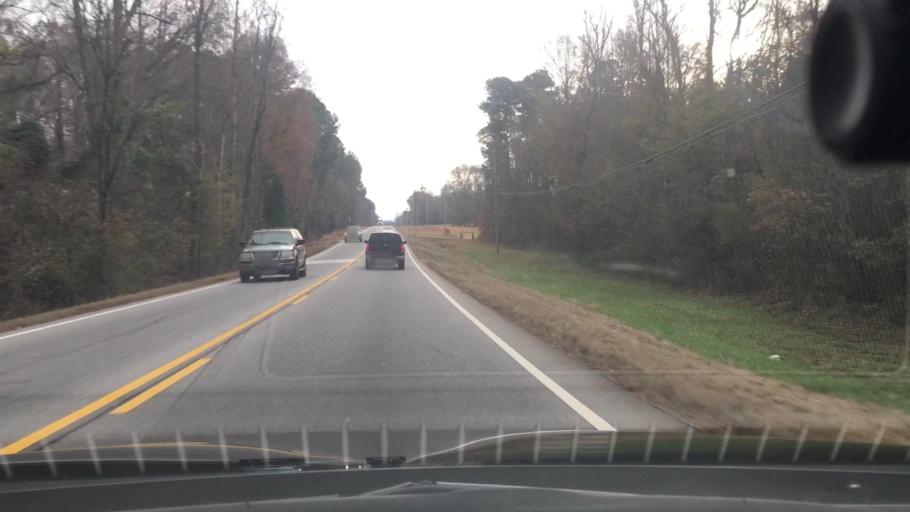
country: US
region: Georgia
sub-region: Coweta County
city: Senoia
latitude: 33.2538
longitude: -84.4862
